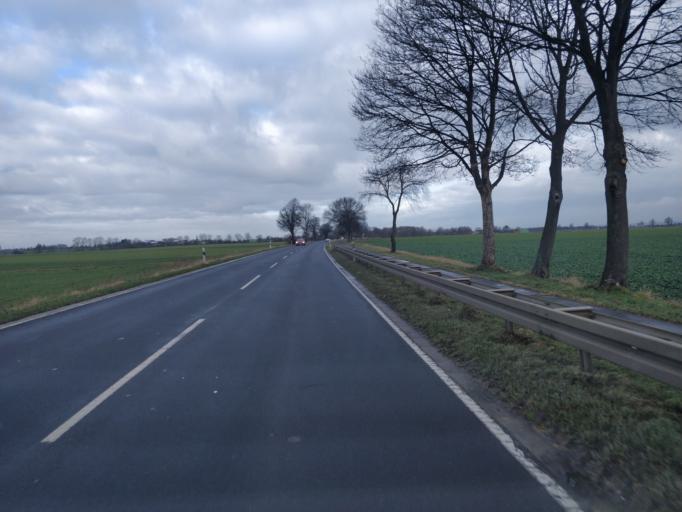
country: DE
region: North Rhine-Westphalia
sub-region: Regierungsbezirk Koln
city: Euskirchen
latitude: 50.6349
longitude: 6.8444
